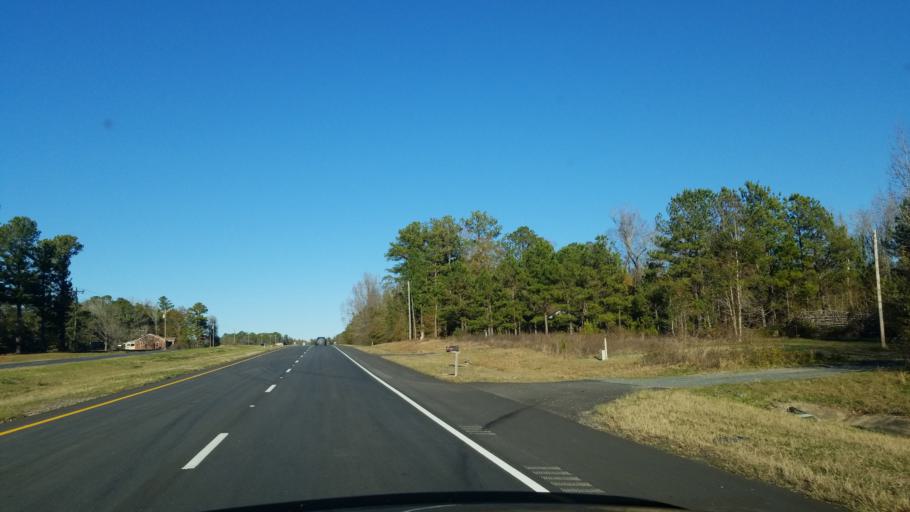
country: US
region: Georgia
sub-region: Talbot County
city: Talbotton
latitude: 32.5668
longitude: -84.6027
